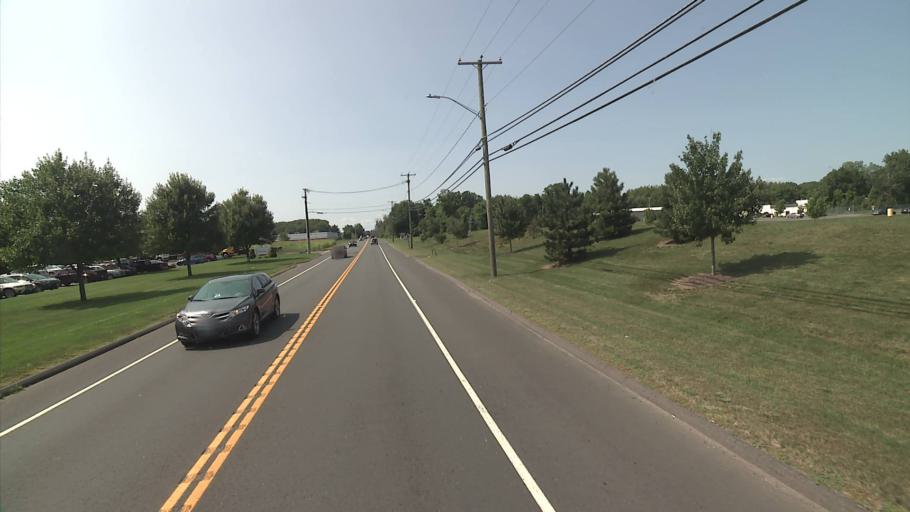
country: US
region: Connecticut
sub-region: Hartford County
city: South Windsor
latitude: 41.8527
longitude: -72.5846
